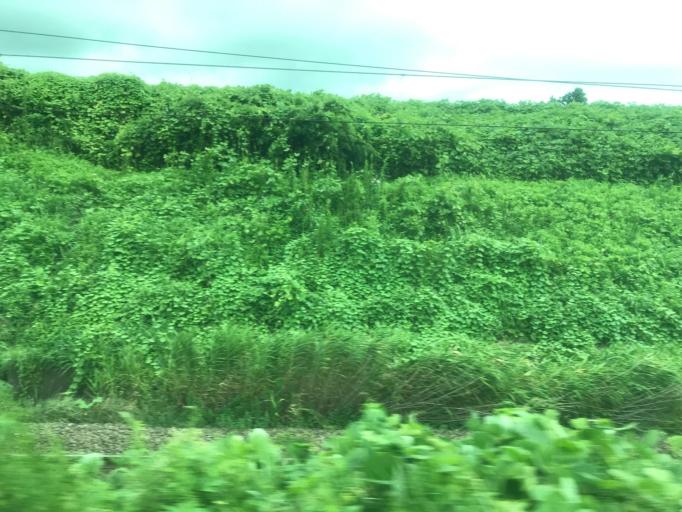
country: JP
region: Fukushima
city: Motomiya
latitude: 37.4620
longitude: 140.3799
